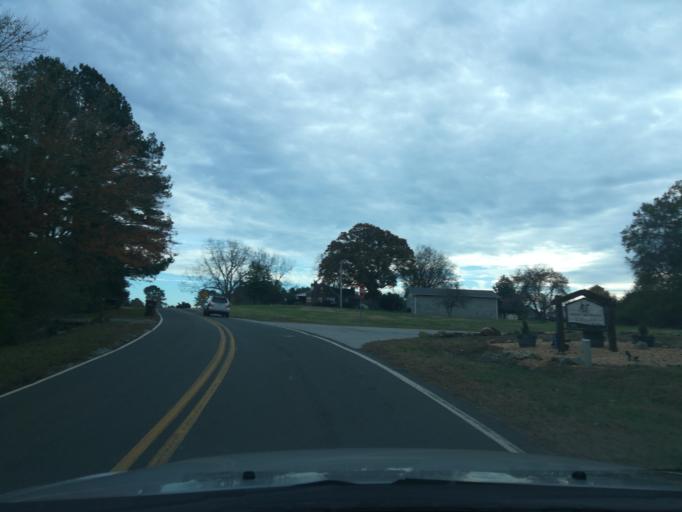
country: US
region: North Carolina
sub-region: Orange County
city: Carrboro
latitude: 35.9795
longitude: -79.0776
